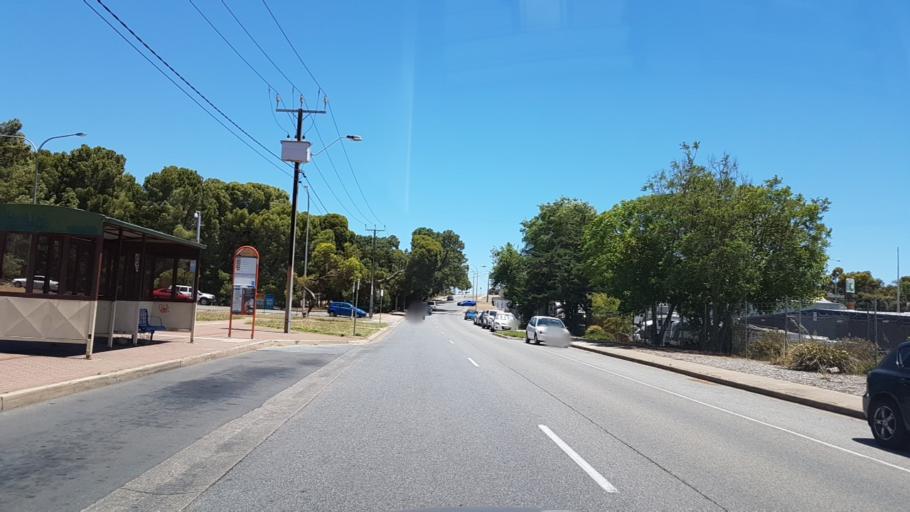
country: AU
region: South Australia
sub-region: Onkaparinga
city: Reynella
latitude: -35.0954
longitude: 138.5378
